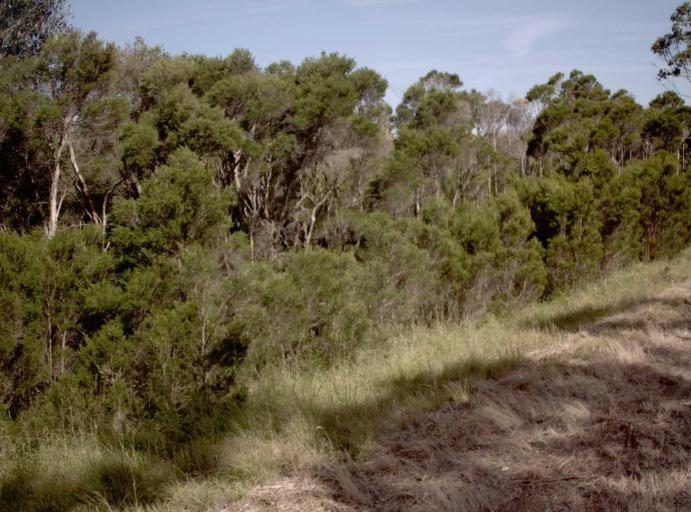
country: AU
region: Victoria
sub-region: Wellington
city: Sale
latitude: -38.2746
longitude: 147.1500
